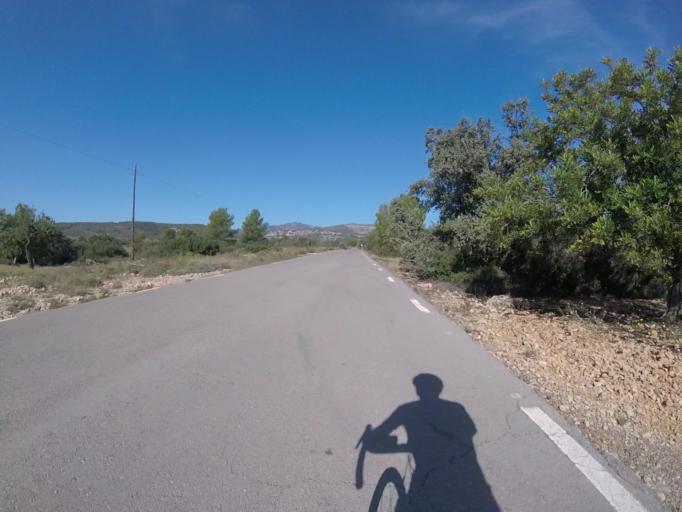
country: ES
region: Valencia
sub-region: Provincia de Castello
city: Sarratella
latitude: 40.2694
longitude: 0.0613
